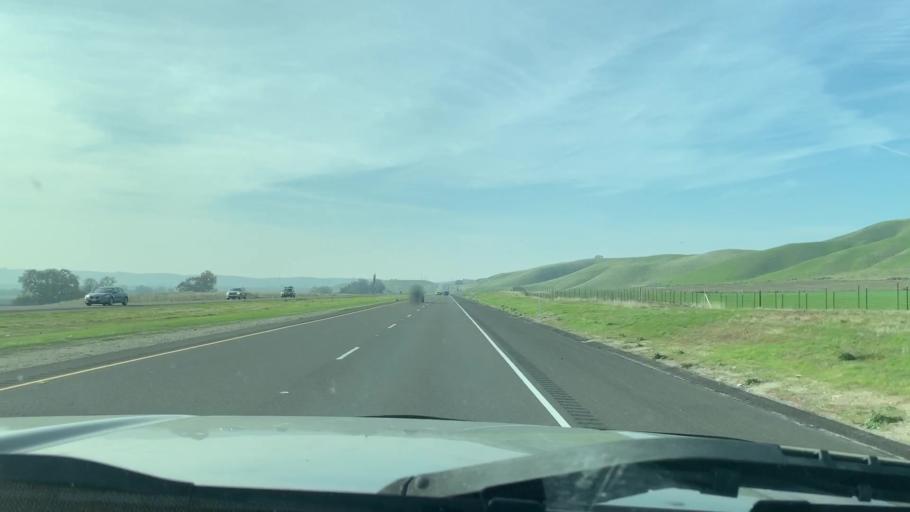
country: US
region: California
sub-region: San Luis Obispo County
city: Shandon
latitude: 35.6612
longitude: -120.4545
